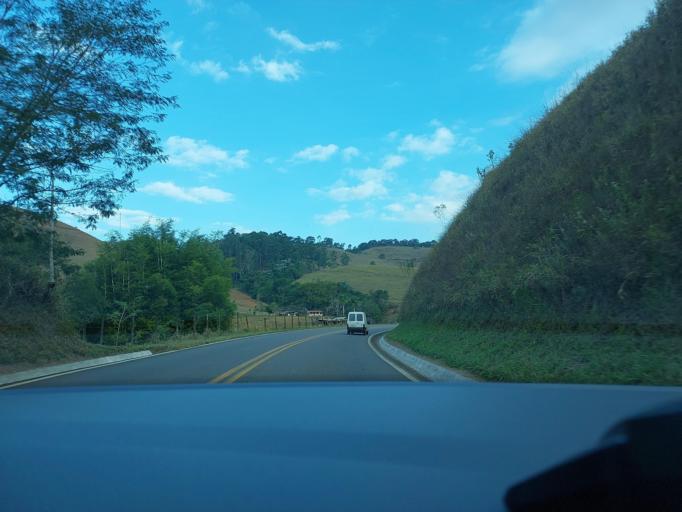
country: BR
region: Minas Gerais
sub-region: Muriae
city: Muriae
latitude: -21.0623
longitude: -42.5025
